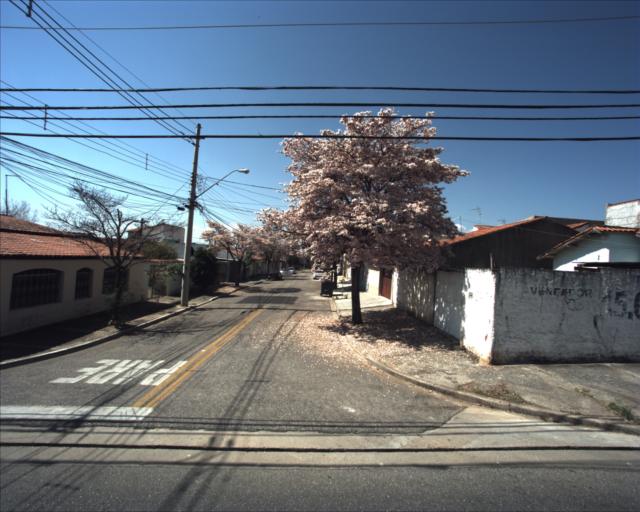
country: BR
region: Sao Paulo
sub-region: Sorocaba
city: Sorocaba
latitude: -23.4981
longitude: -47.5170
